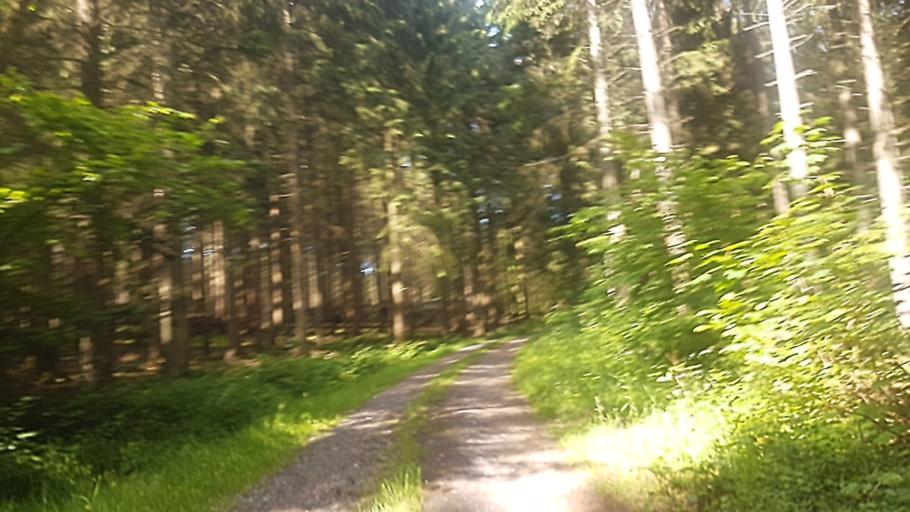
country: BE
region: Wallonia
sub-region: Province de Namur
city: Couvin
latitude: 50.0393
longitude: 4.5730
